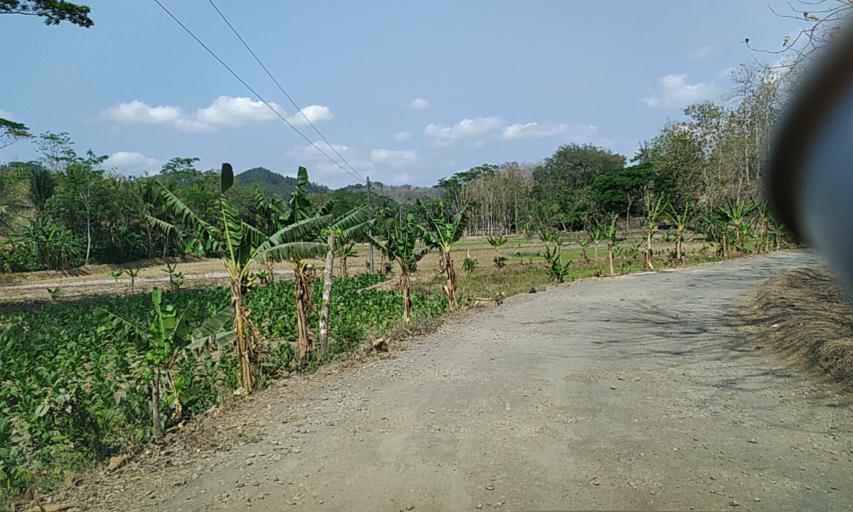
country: ID
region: Central Java
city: Cidadap
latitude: -7.3942
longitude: 108.8602
